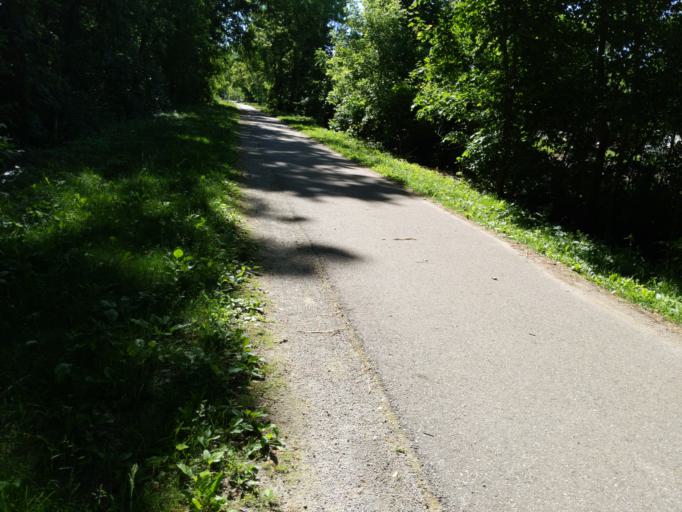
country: US
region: Michigan
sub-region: Livingston County
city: Pinckney
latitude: 42.4608
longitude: -83.9396
